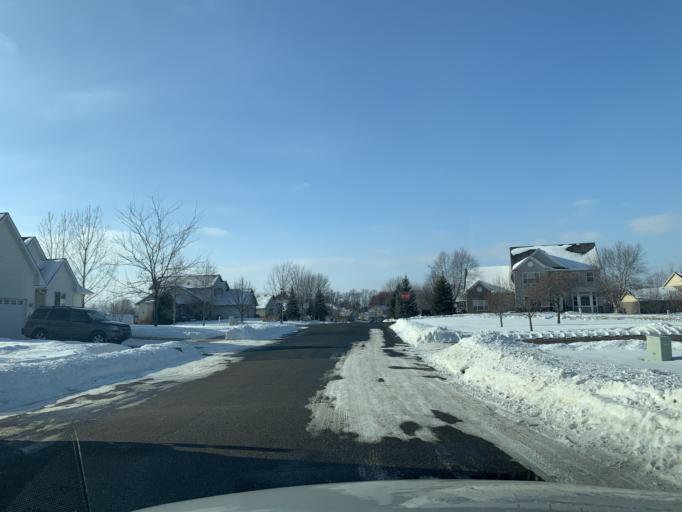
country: US
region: Minnesota
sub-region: Wright County
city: Buffalo
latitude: 45.2020
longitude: -93.8333
